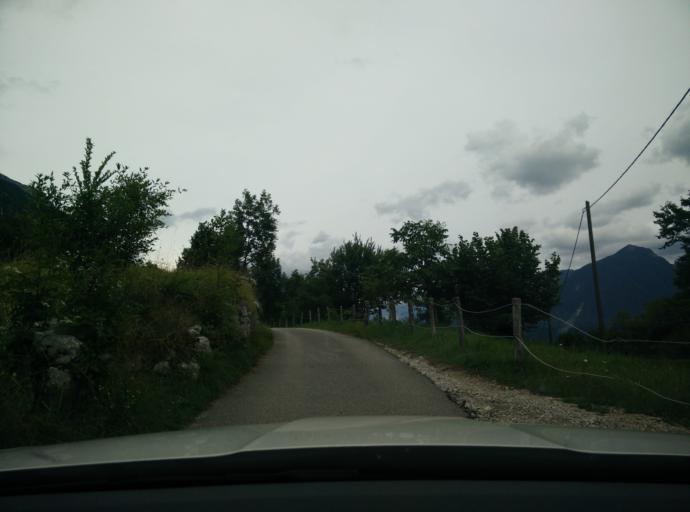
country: SI
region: Bovec
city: Bovec
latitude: 46.3362
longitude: 13.5147
